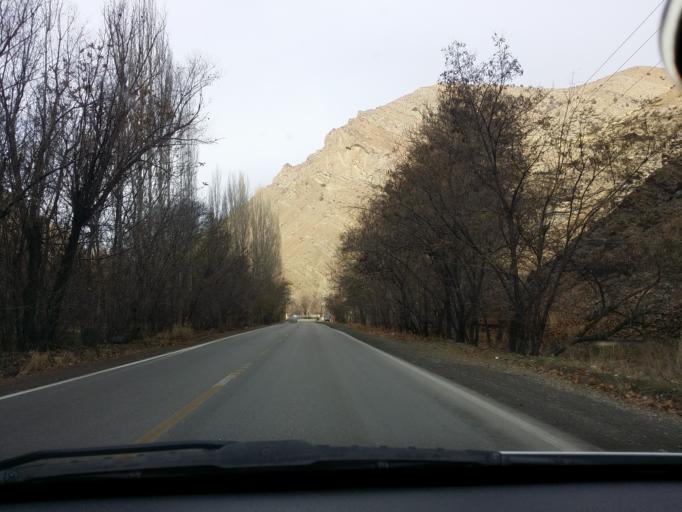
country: IR
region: Tehran
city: Tajrish
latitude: 36.0292
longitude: 51.2252
